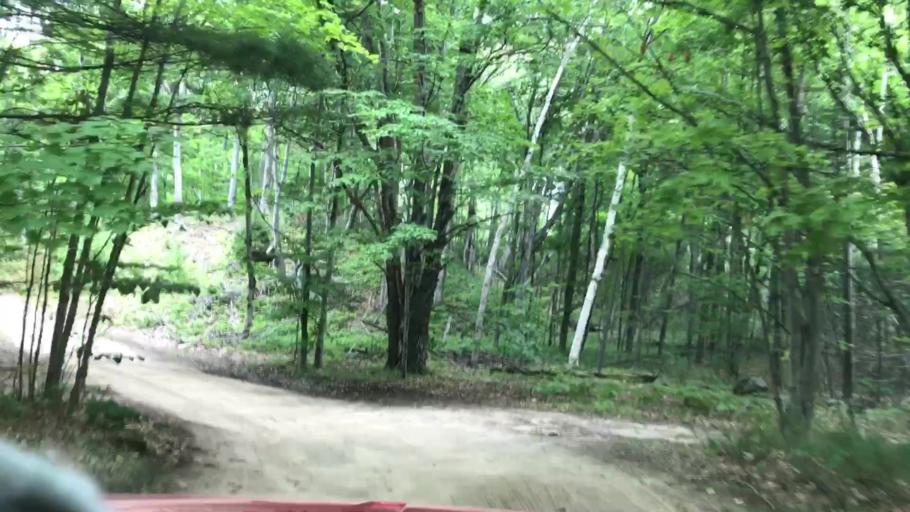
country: US
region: Michigan
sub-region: Charlevoix County
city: Charlevoix
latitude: 45.7217
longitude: -85.5634
